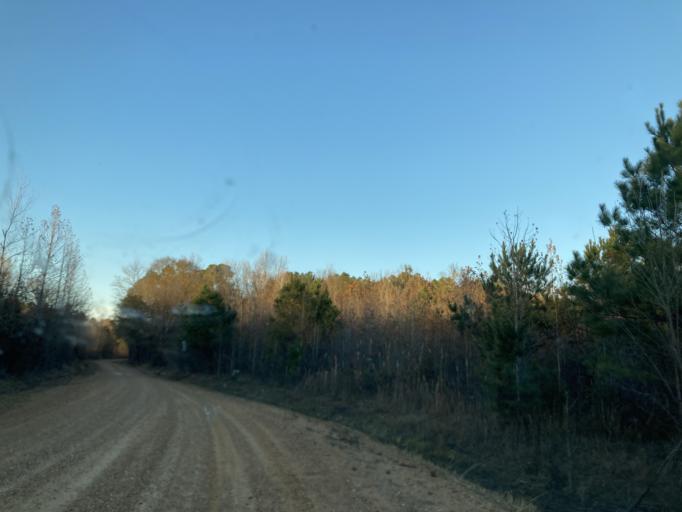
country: US
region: Mississippi
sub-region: Yazoo County
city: Yazoo City
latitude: 32.9730
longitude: -90.2650
